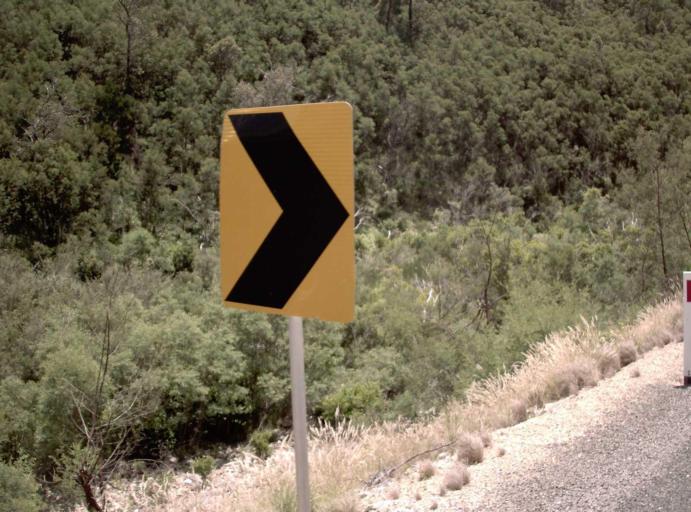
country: AU
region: Victoria
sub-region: East Gippsland
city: Lakes Entrance
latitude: -37.5277
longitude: 147.8469
